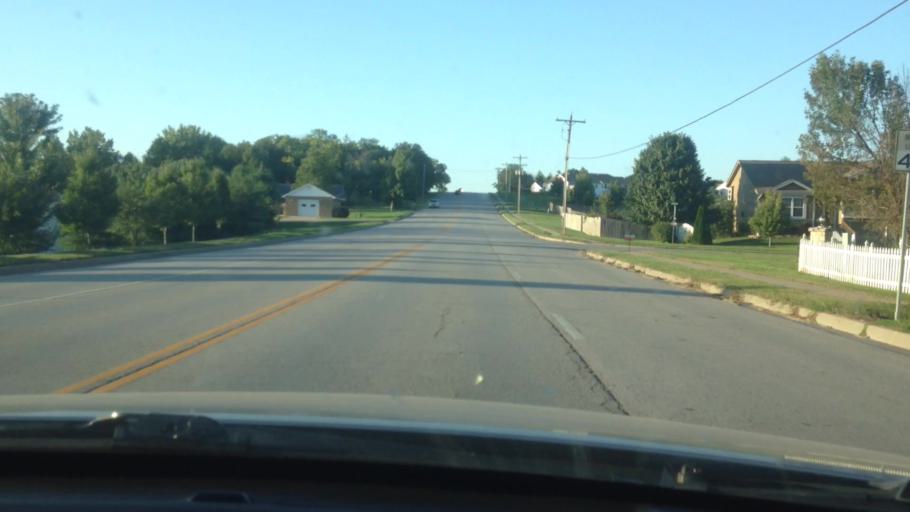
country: US
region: Missouri
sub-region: Platte County
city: Platte City
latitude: 39.3401
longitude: -94.7612
